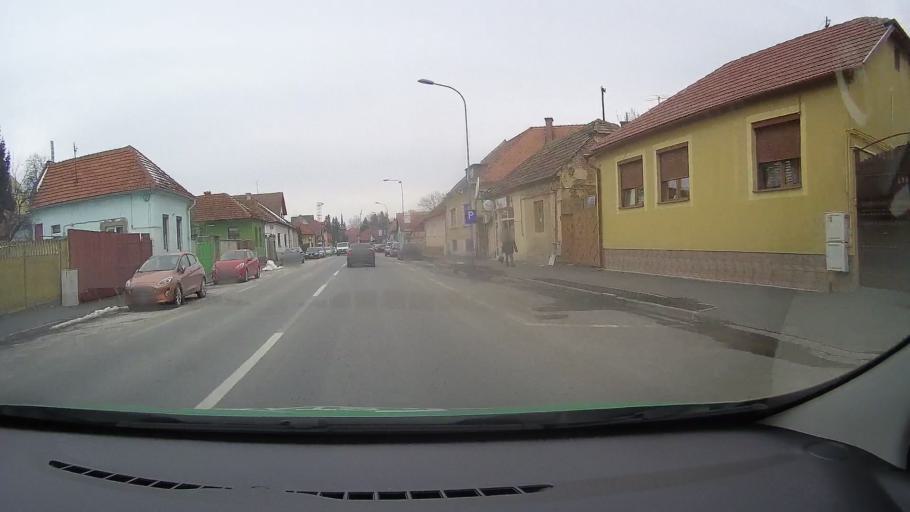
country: RO
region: Brasov
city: Brasov
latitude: 45.6602
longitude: 25.5913
